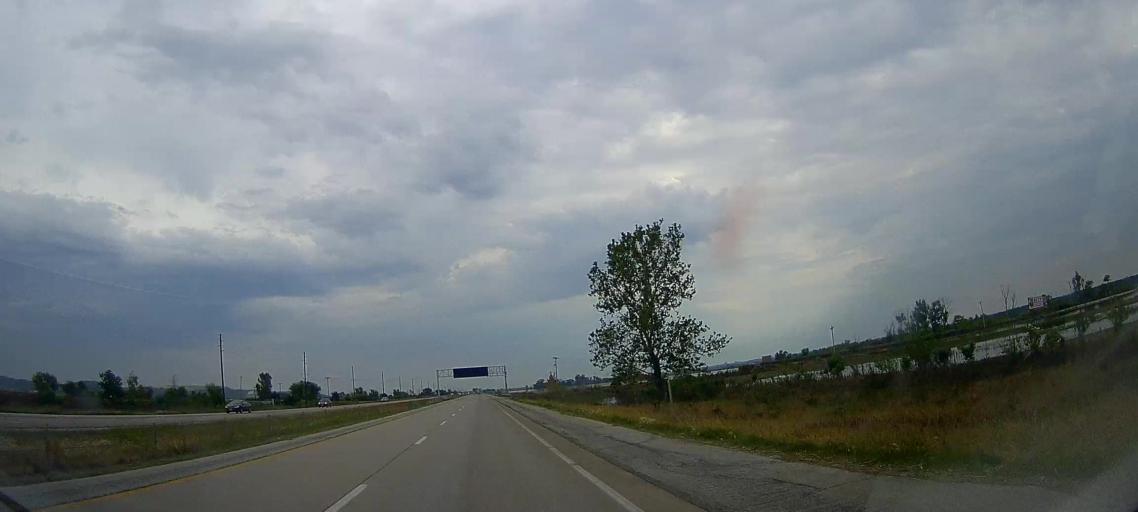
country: US
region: Iowa
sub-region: Pottawattamie County
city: Carter Lake
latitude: 41.3849
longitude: -95.8997
